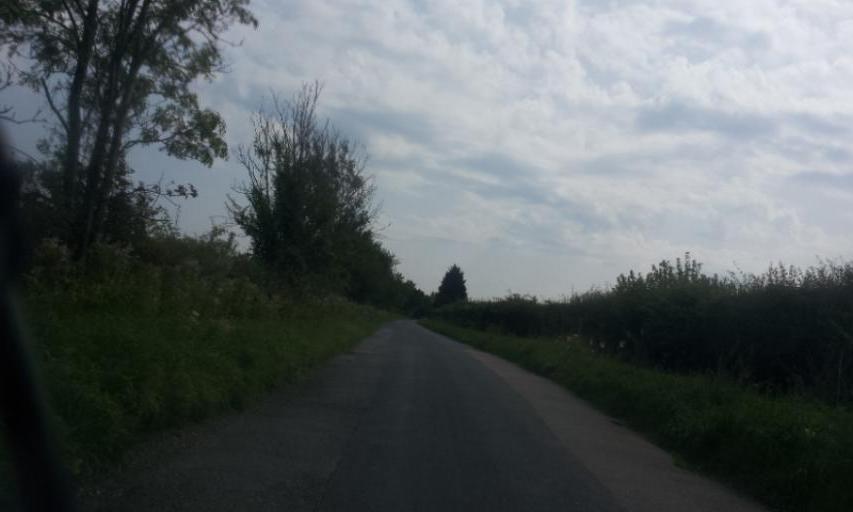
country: GB
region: England
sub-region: Kent
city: Yalding
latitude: 51.1961
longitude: 0.4152
